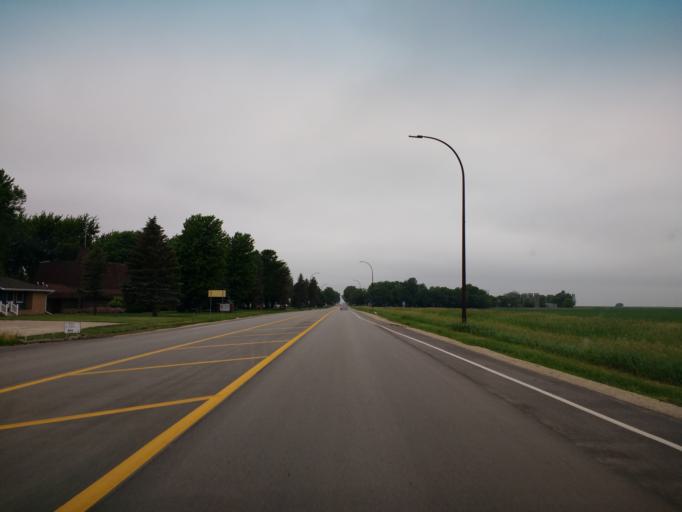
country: US
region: Iowa
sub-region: O'Brien County
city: Sanborn
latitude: 43.1861
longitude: -95.6456
